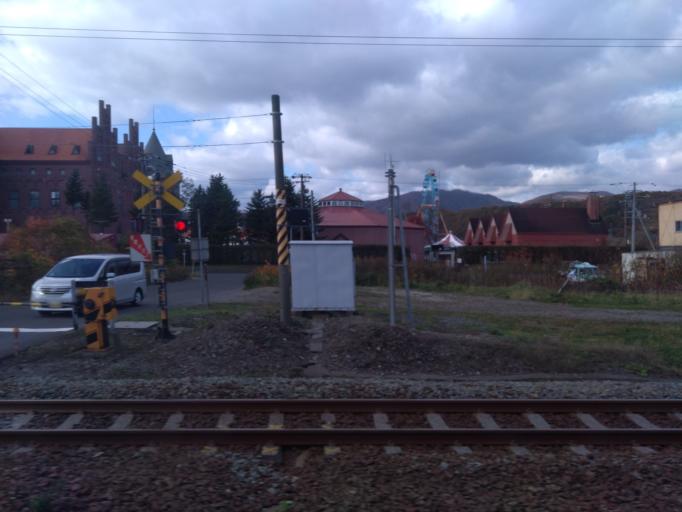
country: JP
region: Hokkaido
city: Shiraoi
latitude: 42.4539
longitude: 141.1841
